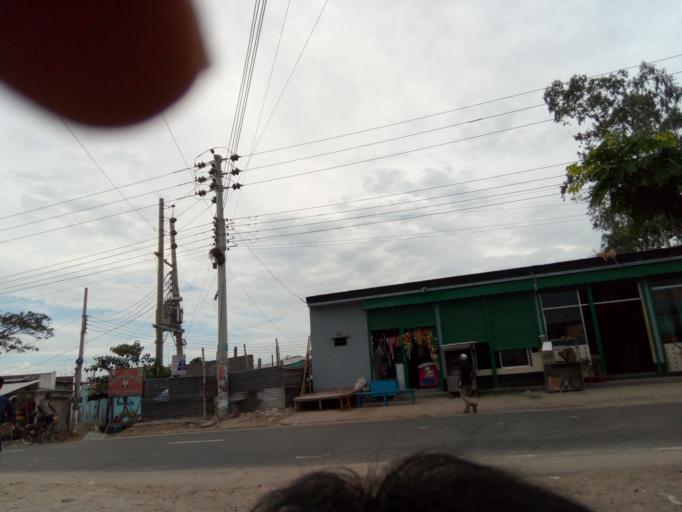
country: BD
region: Dhaka
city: Paltan
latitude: 23.7544
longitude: 90.4501
